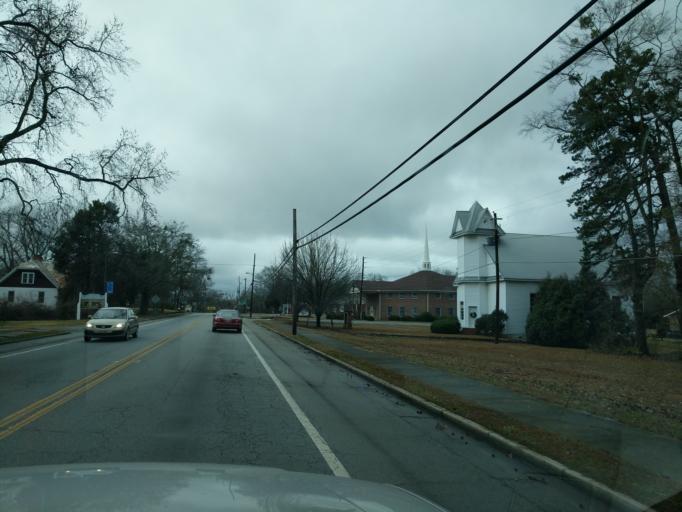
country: US
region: Georgia
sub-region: Hart County
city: Royston
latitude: 34.3441
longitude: -83.1092
